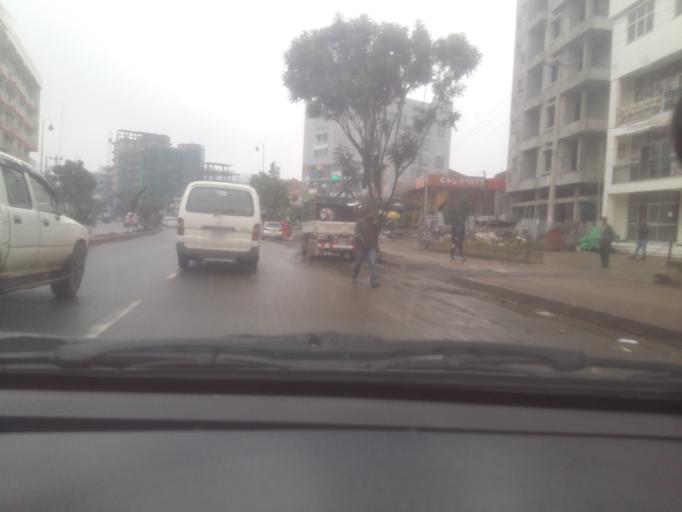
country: ET
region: Adis Abeba
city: Addis Ababa
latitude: 8.9497
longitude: 38.7198
